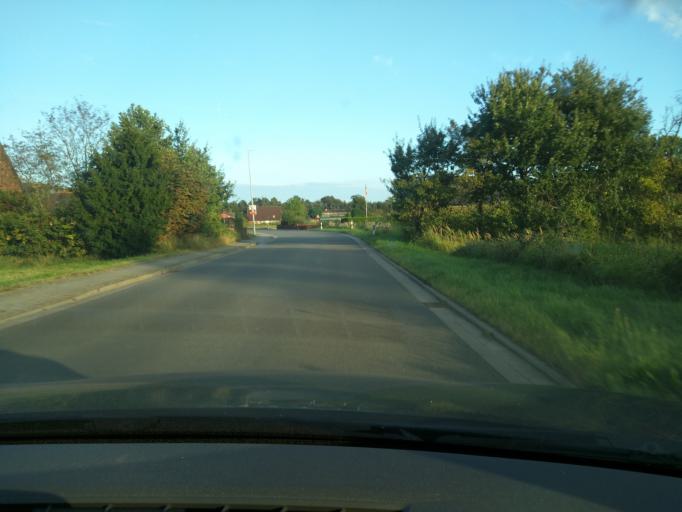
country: DE
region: Lower Saxony
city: Tespe
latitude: 53.3875
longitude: 10.4480
